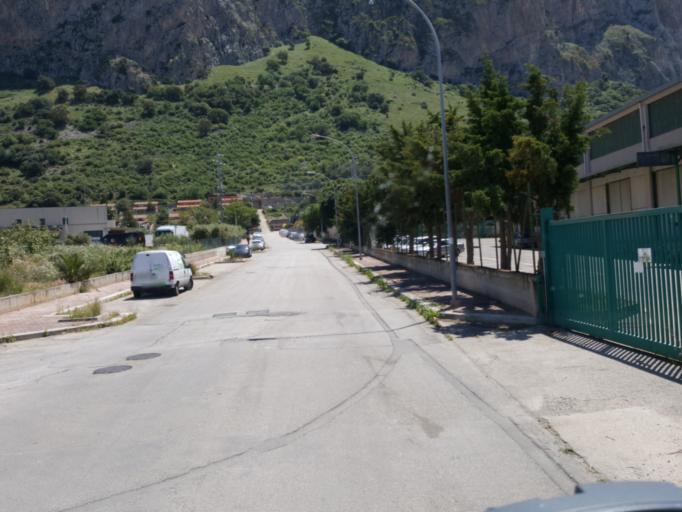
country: IT
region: Sicily
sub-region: Palermo
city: Carini
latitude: 38.1554
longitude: 13.2106
